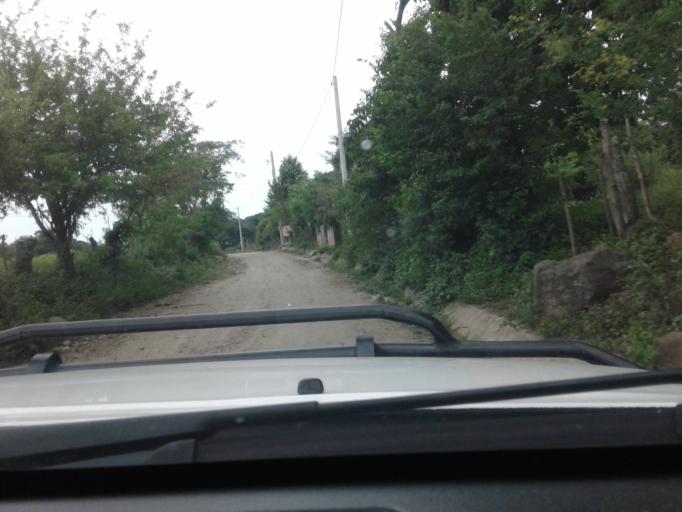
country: NI
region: Matagalpa
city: Ciudad Dario
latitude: 12.9029
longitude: -86.2028
